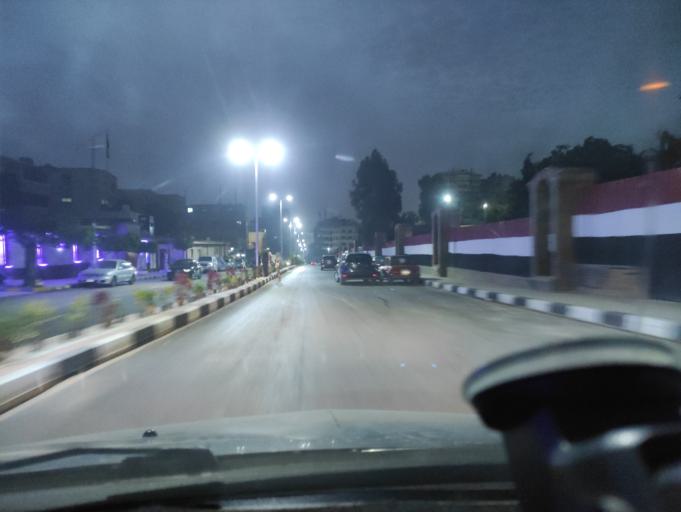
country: EG
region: Muhafazat al Qahirah
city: Cairo
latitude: 30.0465
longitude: 31.3370
